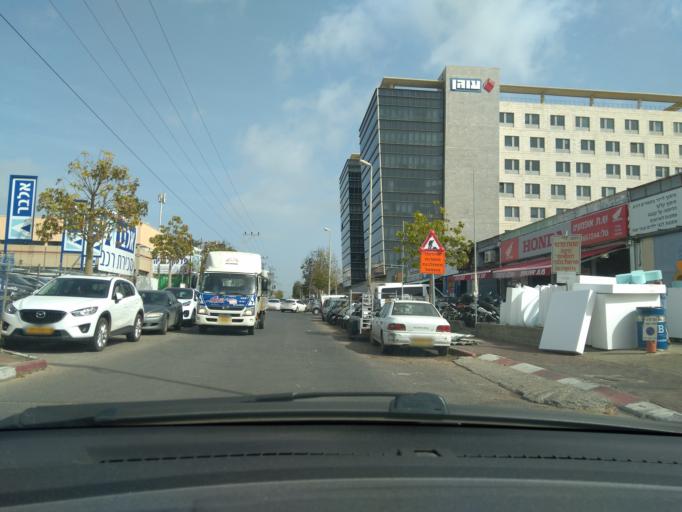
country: IL
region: Central District
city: Even Yehuda
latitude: 32.2765
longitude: 34.8580
